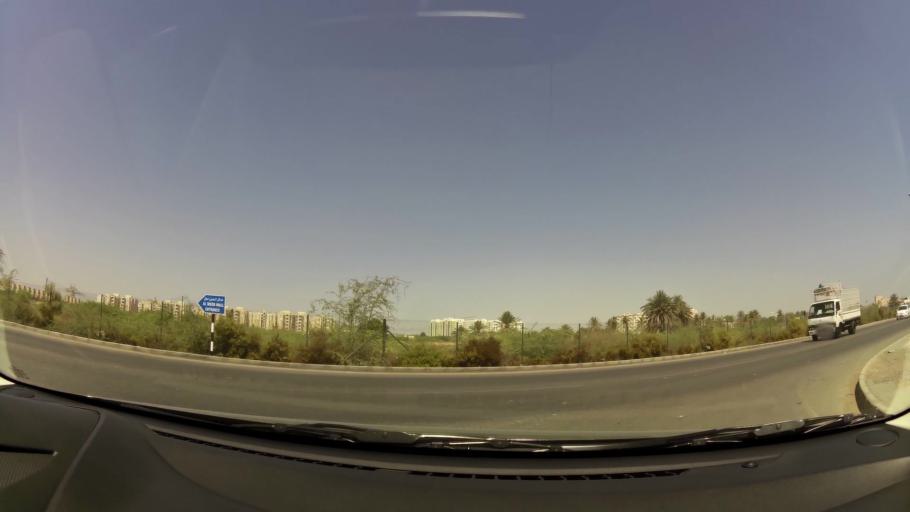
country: OM
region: Muhafazat Masqat
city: As Sib al Jadidah
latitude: 23.6232
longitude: 58.2486
